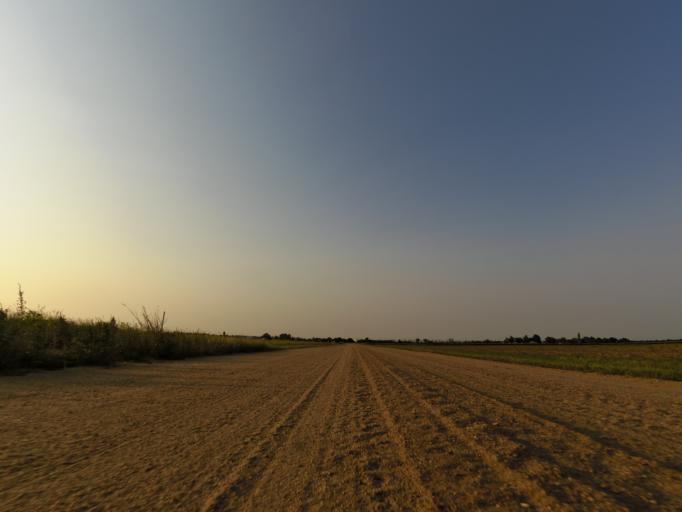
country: US
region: Kansas
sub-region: Reno County
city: South Hutchinson
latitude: 37.9782
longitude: -97.9957
